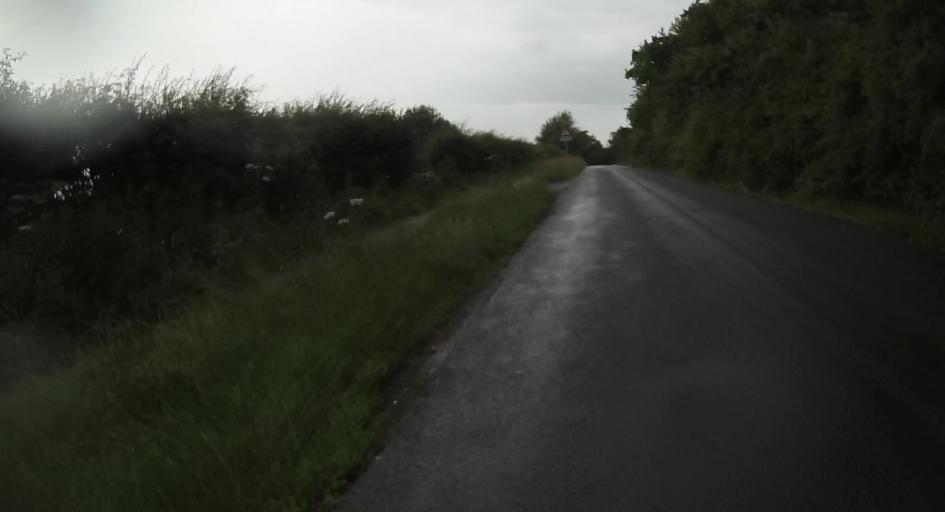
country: GB
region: England
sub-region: Hampshire
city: Odiham
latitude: 51.2475
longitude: -0.9510
